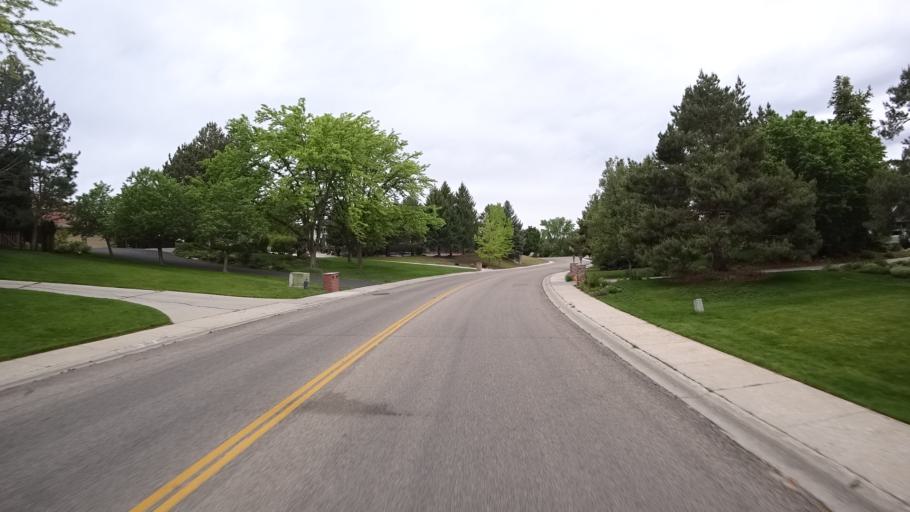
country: US
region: Idaho
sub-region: Ada County
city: Boise
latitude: 43.6162
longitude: -116.1672
